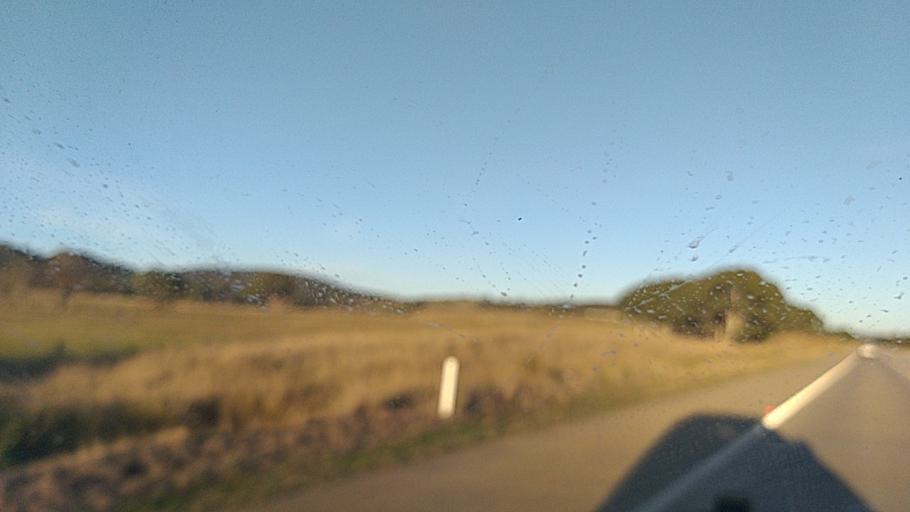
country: AU
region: New South Wales
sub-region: Yass Valley
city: Gundaroo
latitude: -34.9003
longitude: 149.4750
